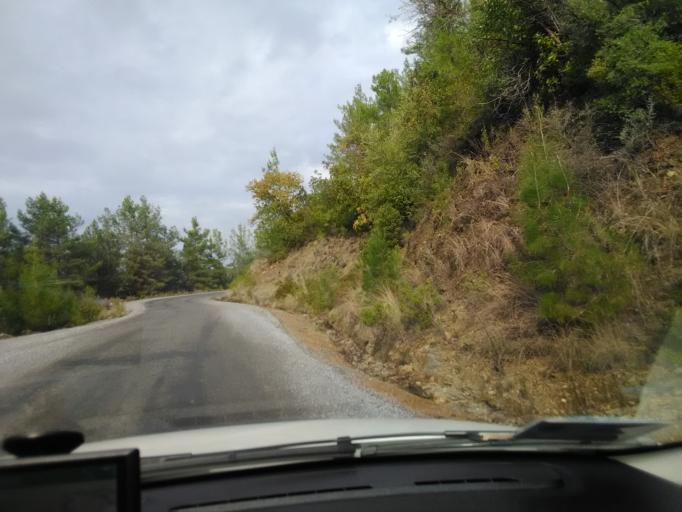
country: TR
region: Antalya
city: Gazipasa
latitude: 36.2455
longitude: 32.4206
